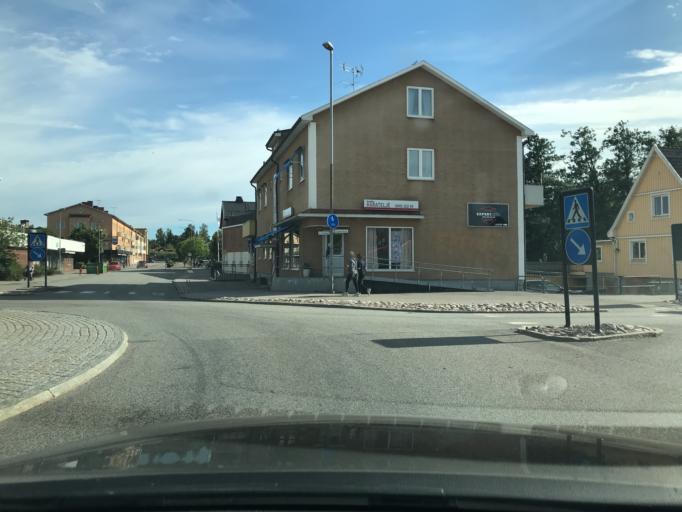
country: SE
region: Kalmar
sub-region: Hultsfreds Kommun
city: Hultsfred
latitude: 57.4890
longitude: 15.8409
